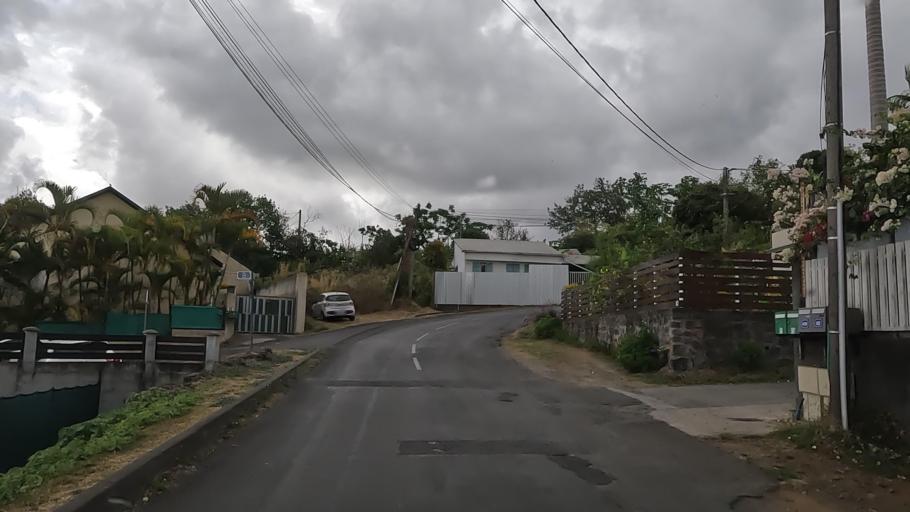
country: RE
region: Reunion
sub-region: Reunion
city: Le Tampon
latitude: -21.2737
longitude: 55.5032
